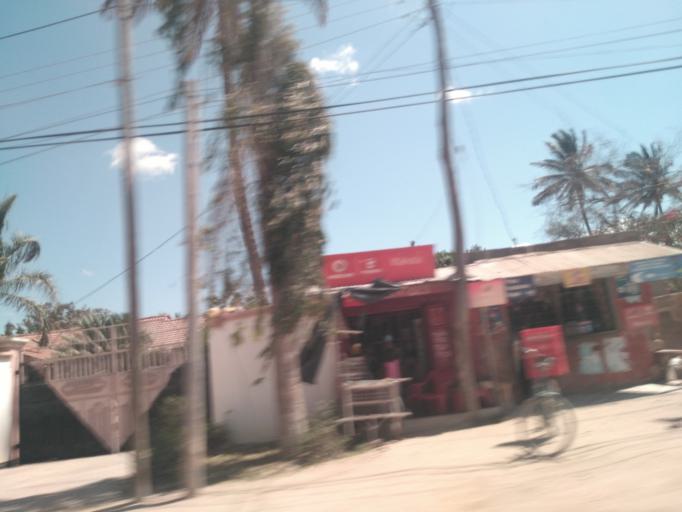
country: TZ
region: Dodoma
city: Dodoma
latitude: -6.1650
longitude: 35.7662
